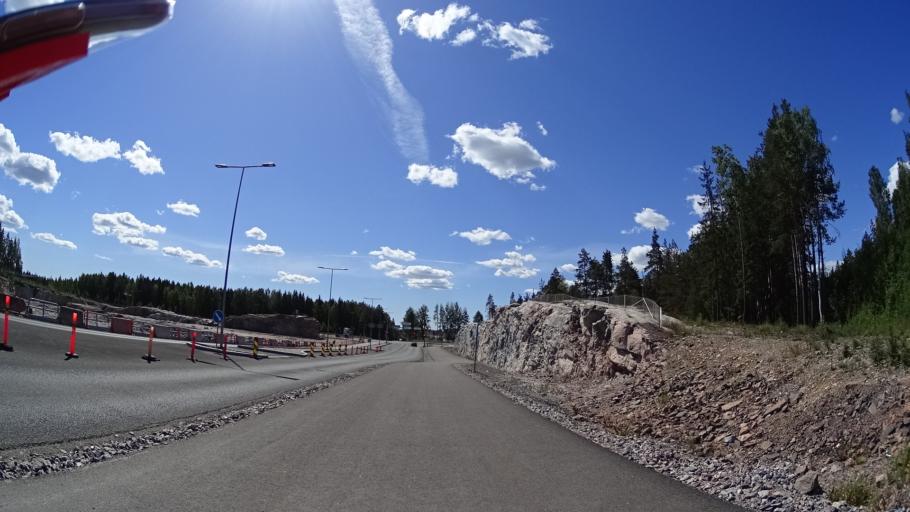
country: FI
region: Uusimaa
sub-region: Helsinki
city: Vantaa
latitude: 60.3038
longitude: 24.9512
